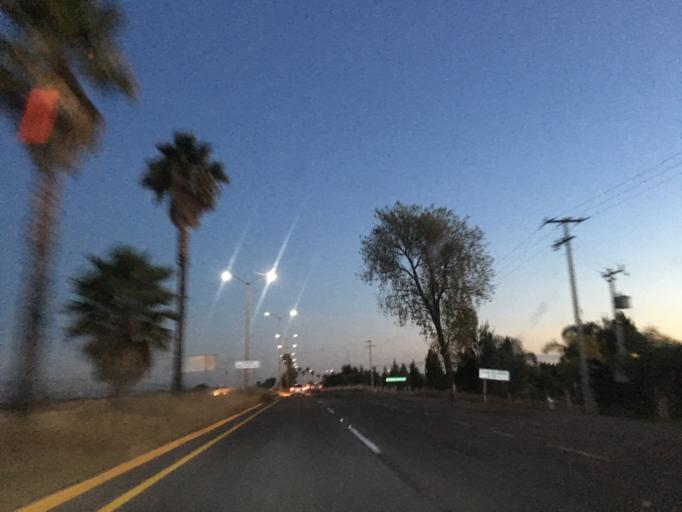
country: MX
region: Aguascalientes
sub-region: Aguascalientes
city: Penuelas (El Cienegal)
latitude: 21.7205
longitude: -102.3101
